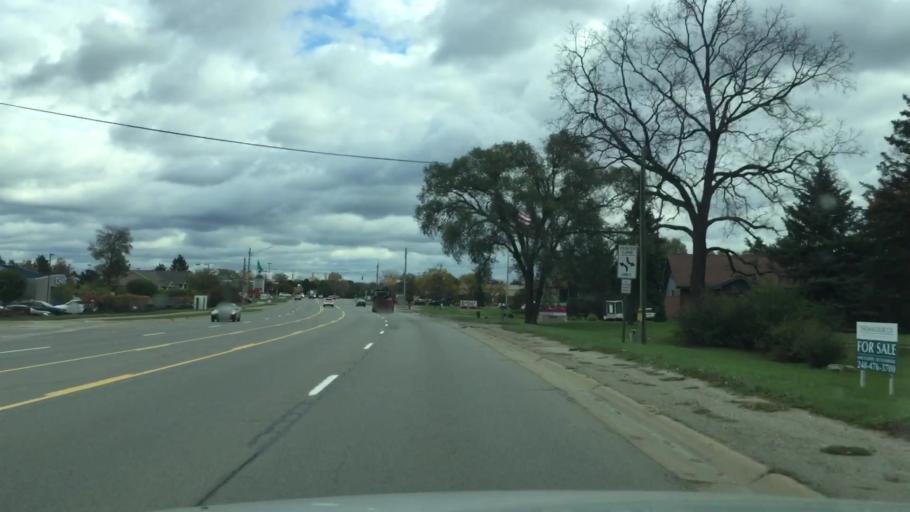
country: US
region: Michigan
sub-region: Oakland County
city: Waterford
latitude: 42.6563
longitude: -83.4707
